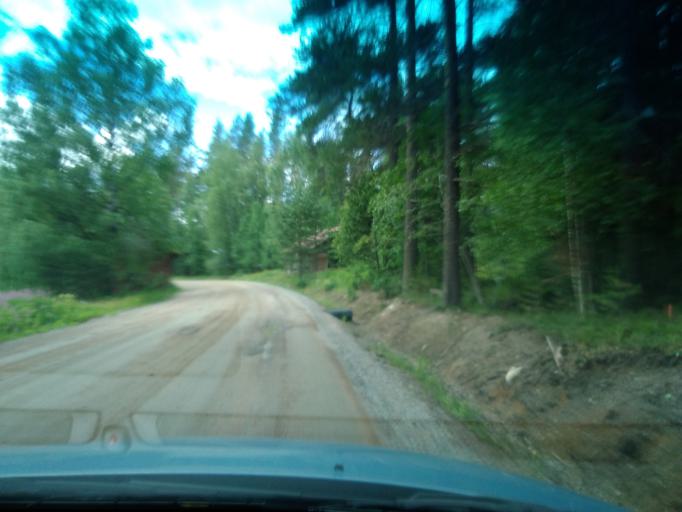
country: FI
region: Central Finland
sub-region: Saarijaervi-Viitasaari
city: Karstula
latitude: 62.8013
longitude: 24.9893
